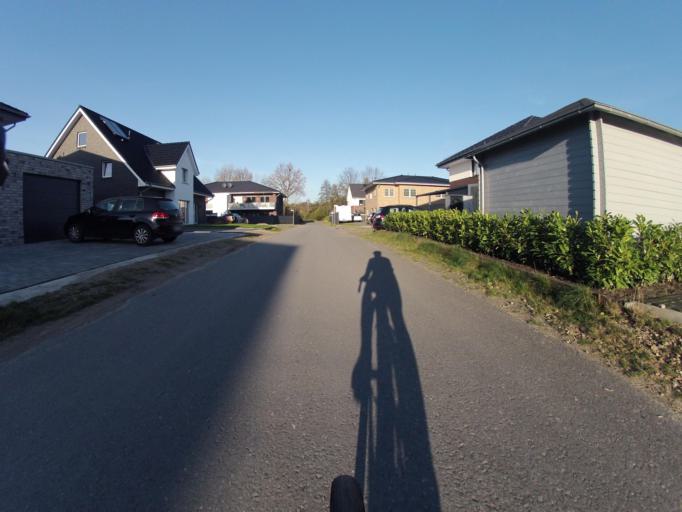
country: DE
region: North Rhine-Westphalia
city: Ibbenburen
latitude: 52.2783
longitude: 7.6934
